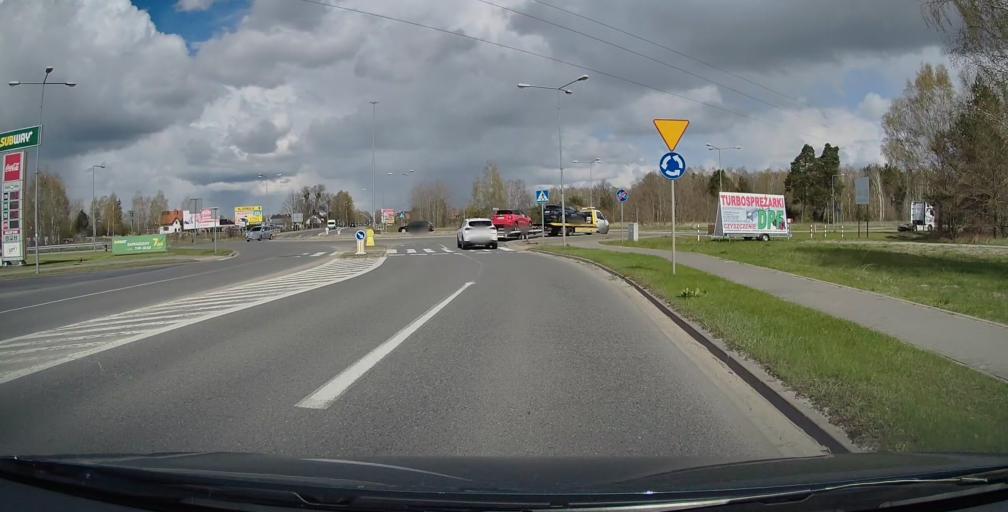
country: PL
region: Masovian Voivodeship
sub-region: Ostroleka
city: Ostroleka
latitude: 53.0616
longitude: 21.5835
